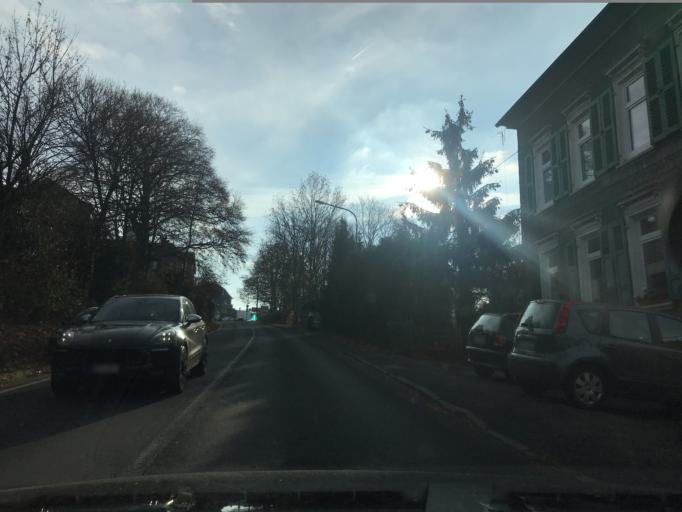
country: DE
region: North Rhine-Westphalia
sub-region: Regierungsbezirk Dusseldorf
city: Remscheid
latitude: 51.1993
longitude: 7.1622
